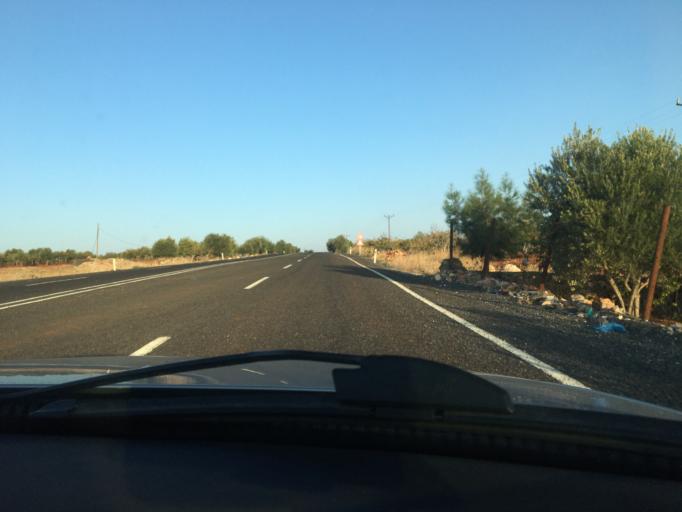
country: TR
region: Sanliurfa
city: Halfeti
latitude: 37.2435
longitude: 37.8897
